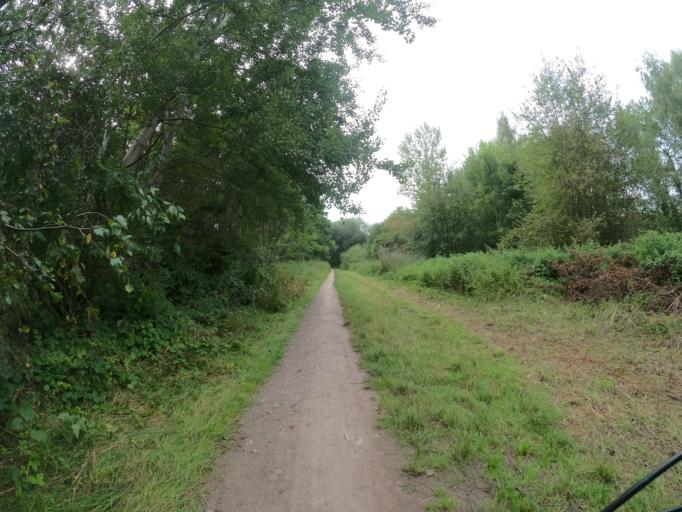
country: DE
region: North Rhine-Westphalia
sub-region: Regierungsbezirk Arnsberg
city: Lippstadt
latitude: 51.6909
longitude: 8.3166
